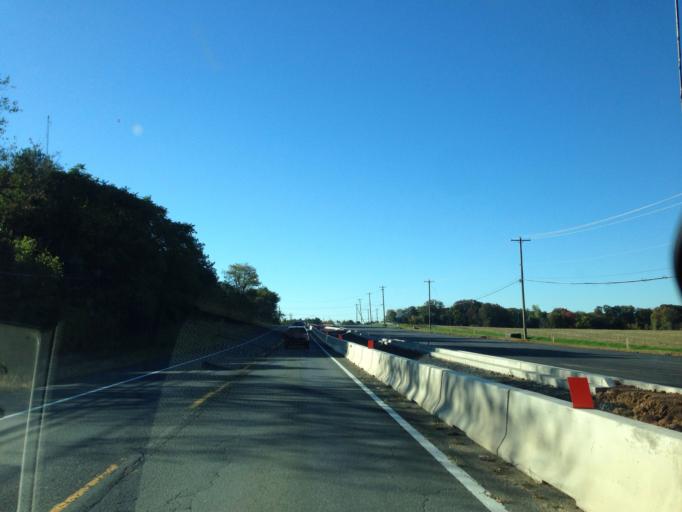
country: US
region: Maryland
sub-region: Montgomery County
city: Clarksburg
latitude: 39.2147
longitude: -77.2390
